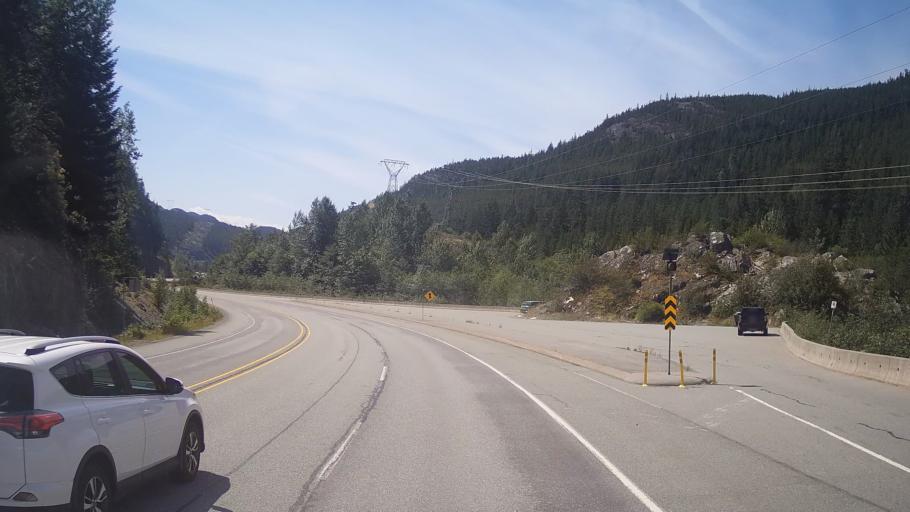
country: CA
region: British Columbia
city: Whistler
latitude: 49.9413
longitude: -123.1672
